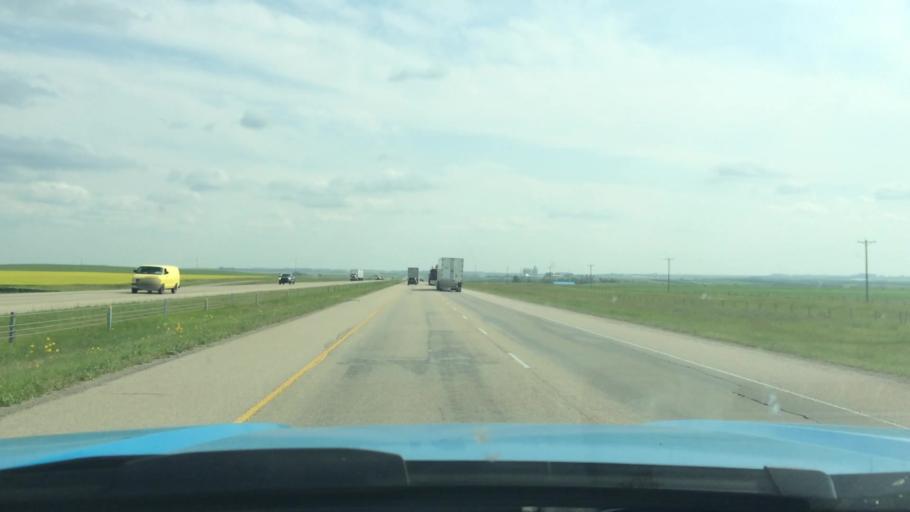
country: CA
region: Alberta
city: Carstairs
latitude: 51.5310
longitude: -114.0253
